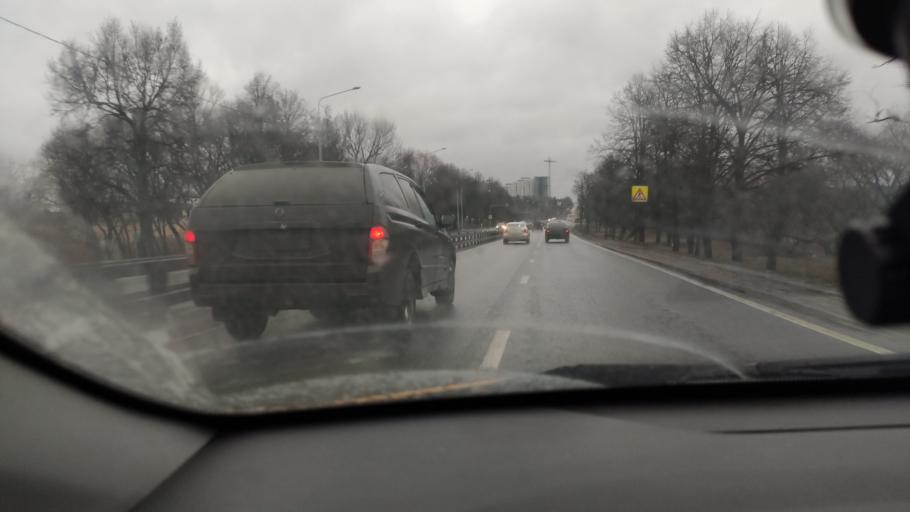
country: RU
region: Moskovskaya
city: Dubrovitsy
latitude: 55.4031
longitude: 37.4556
